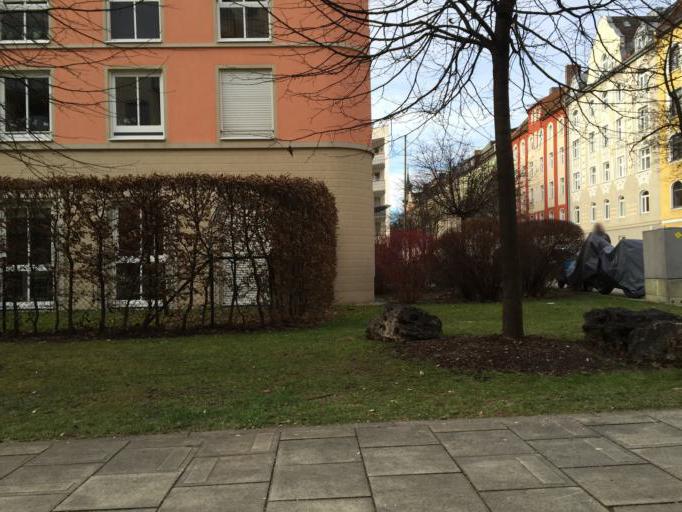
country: DE
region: Bavaria
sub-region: Upper Bavaria
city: Bogenhausen
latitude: 48.1329
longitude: 11.6075
